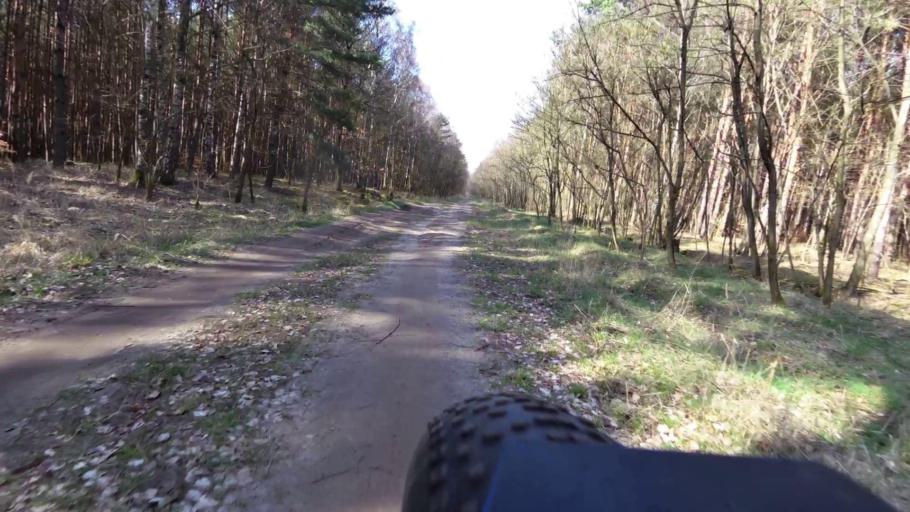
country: PL
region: Lubusz
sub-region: Powiat slubicki
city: Cybinka
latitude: 52.2152
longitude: 14.8536
